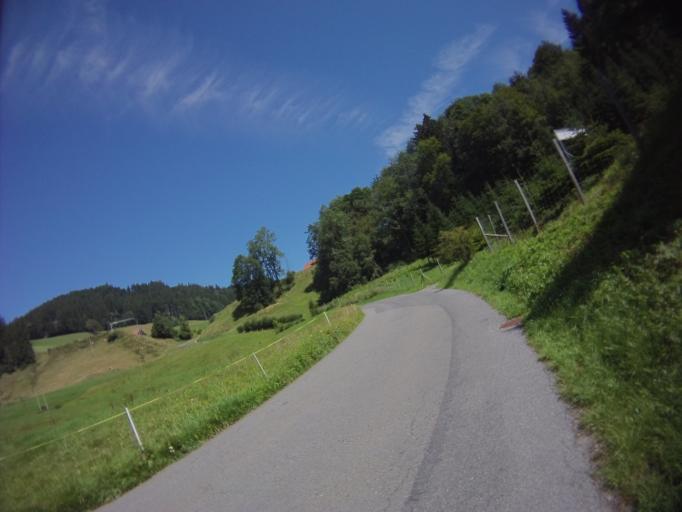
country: CH
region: Schwyz
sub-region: Bezirk Hoefe
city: Feusisberg
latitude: 47.1704
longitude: 8.7678
